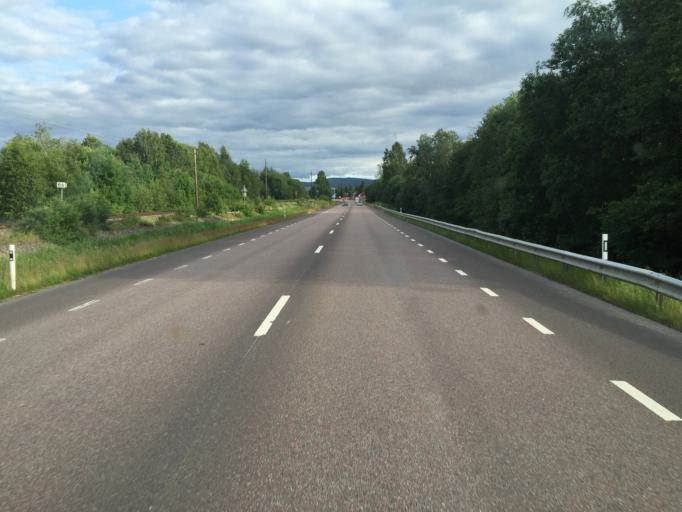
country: SE
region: Dalarna
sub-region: Gagnefs Kommun
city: Djuras
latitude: 60.5702
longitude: 15.1254
